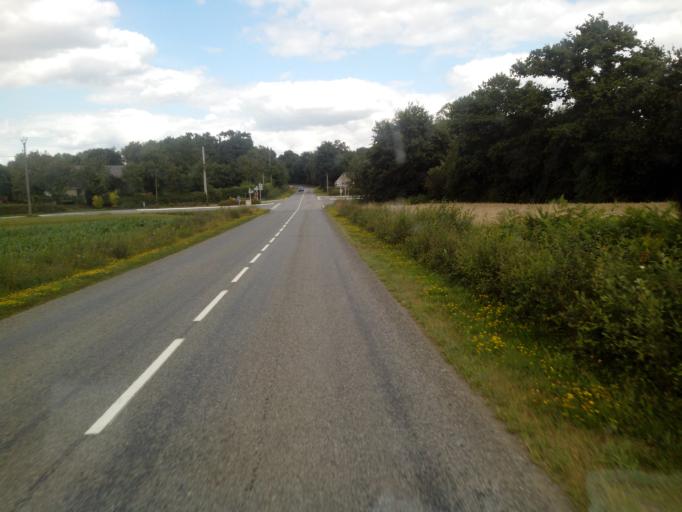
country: FR
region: Brittany
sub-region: Departement du Morbihan
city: Josselin
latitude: 47.9908
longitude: -2.5118
